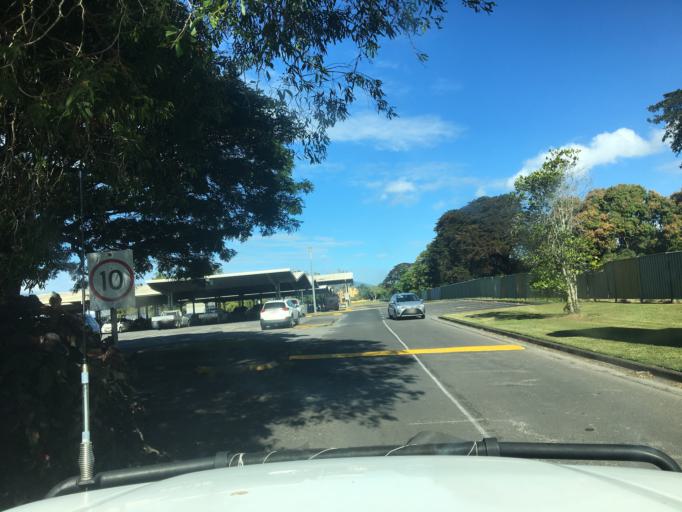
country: AU
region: Queensland
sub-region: Cairns
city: Woree
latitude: -16.9264
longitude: 145.7393
